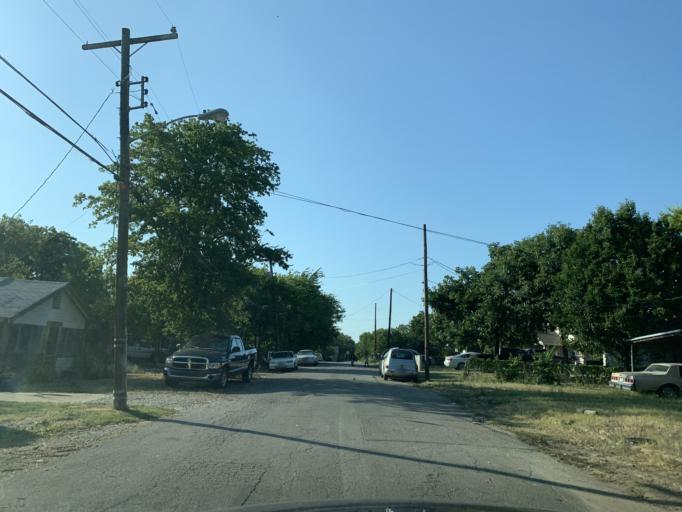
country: US
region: Texas
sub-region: Dallas County
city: Dallas
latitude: 32.7019
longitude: -96.7963
